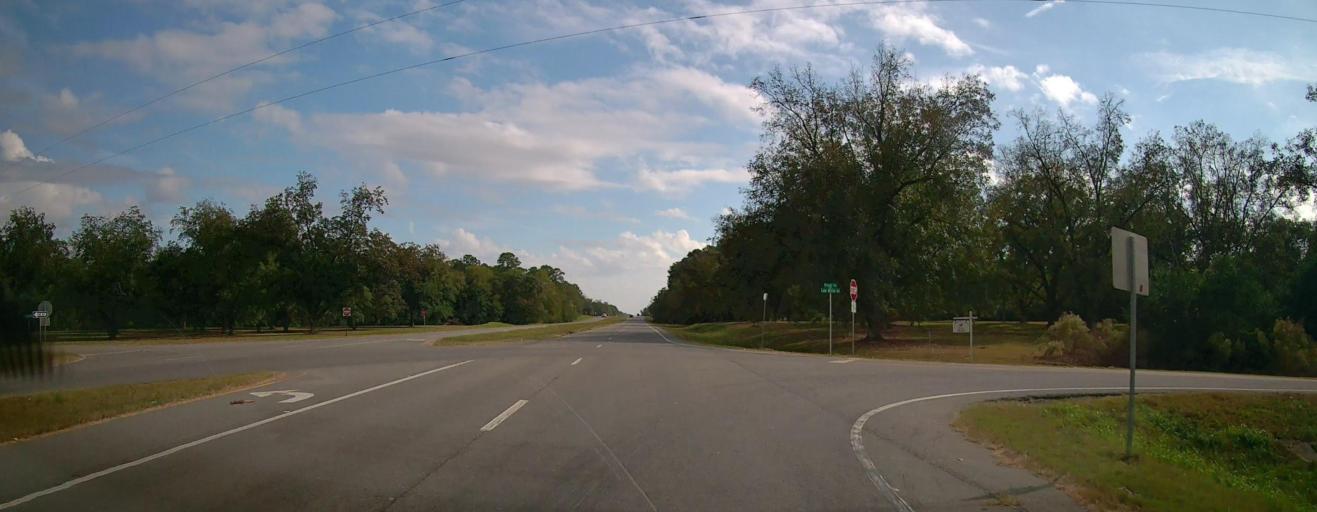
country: US
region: Georgia
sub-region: Thomas County
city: Meigs
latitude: 31.0141
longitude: -84.0546
